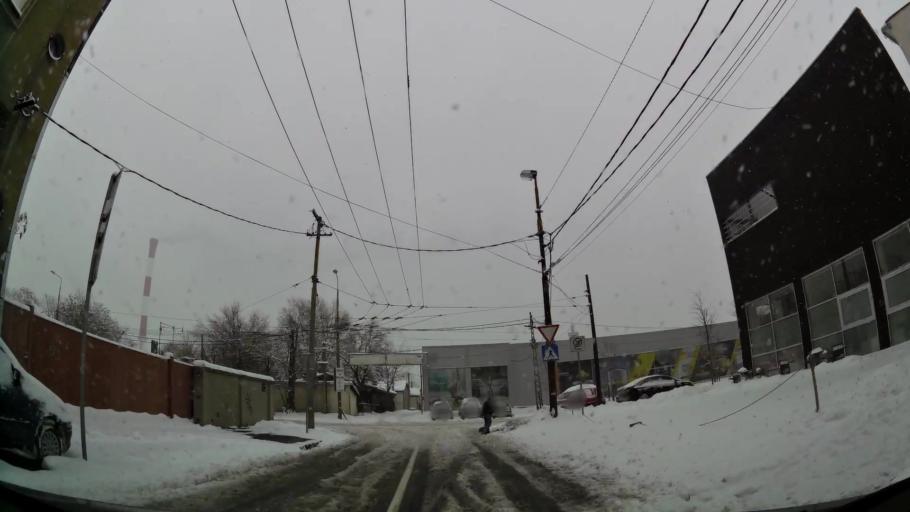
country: RS
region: Central Serbia
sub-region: Belgrade
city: Stari Grad
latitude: 44.8235
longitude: 20.4682
